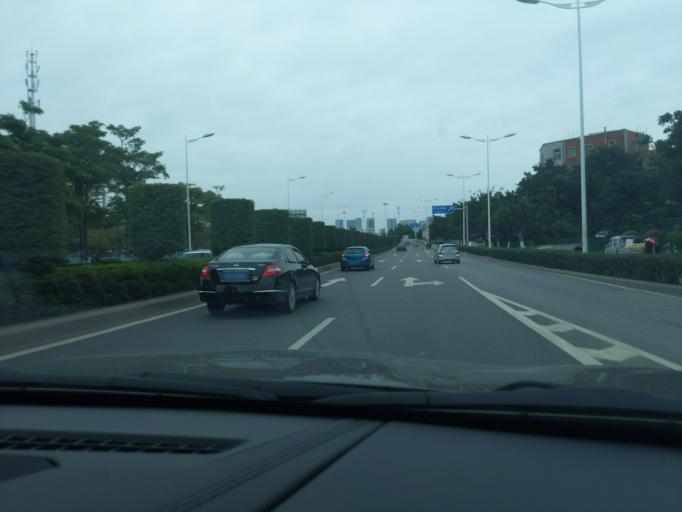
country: CN
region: Fujian
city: Liuwudian
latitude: 24.5316
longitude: 118.1647
